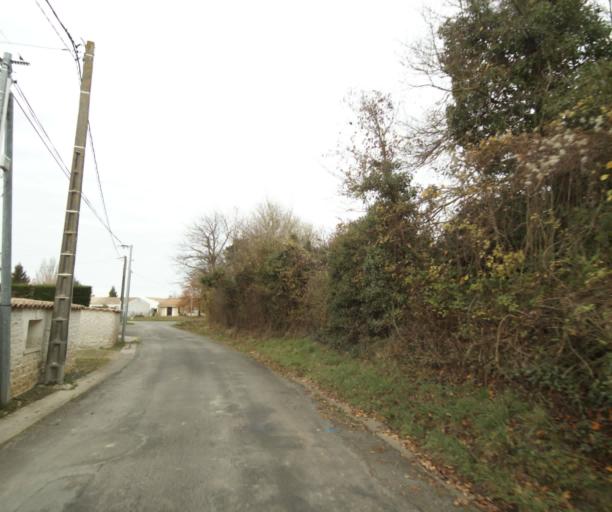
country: FR
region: Poitou-Charentes
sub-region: Departement de la Charente-Maritime
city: Corme-Royal
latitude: 45.7354
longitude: -0.7860
